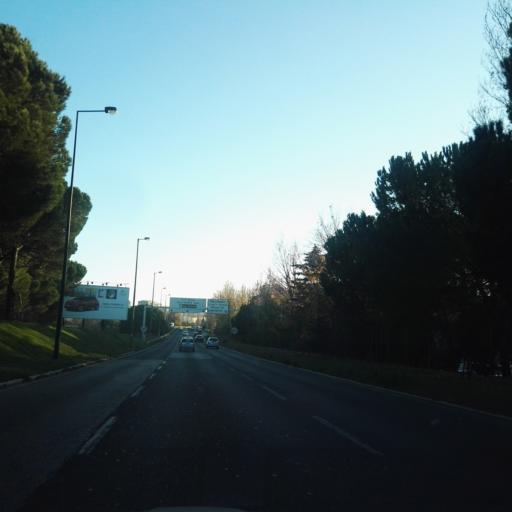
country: PT
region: Lisbon
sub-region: Loures
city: Moscavide
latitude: 38.7737
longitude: -9.1239
